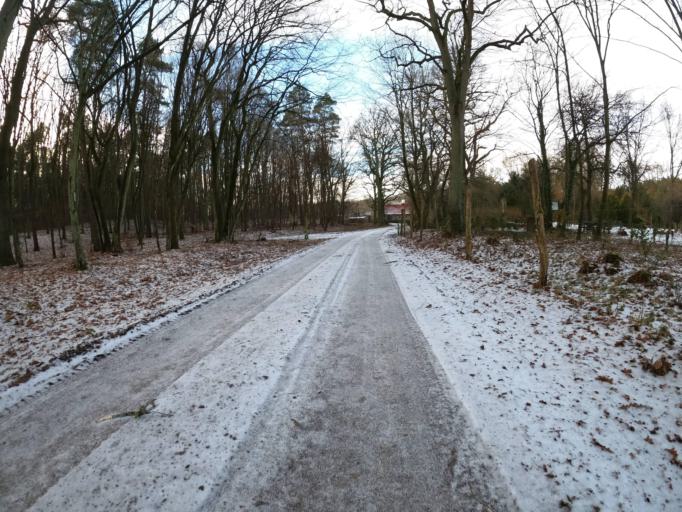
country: PL
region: Lubusz
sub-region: Powiat slubicki
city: Rzepin
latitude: 52.3068
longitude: 14.8144
